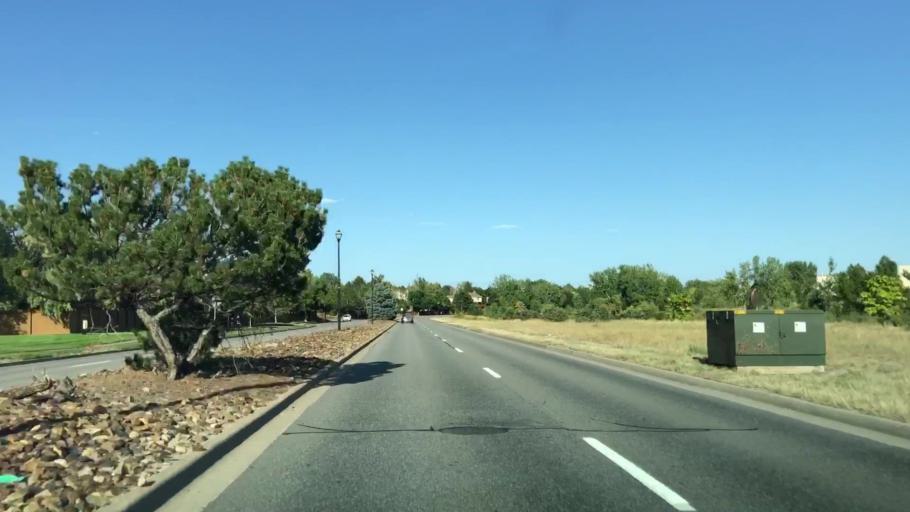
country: US
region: Colorado
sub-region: Arapahoe County
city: Dove Valley
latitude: 39.6107
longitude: -104.8003
